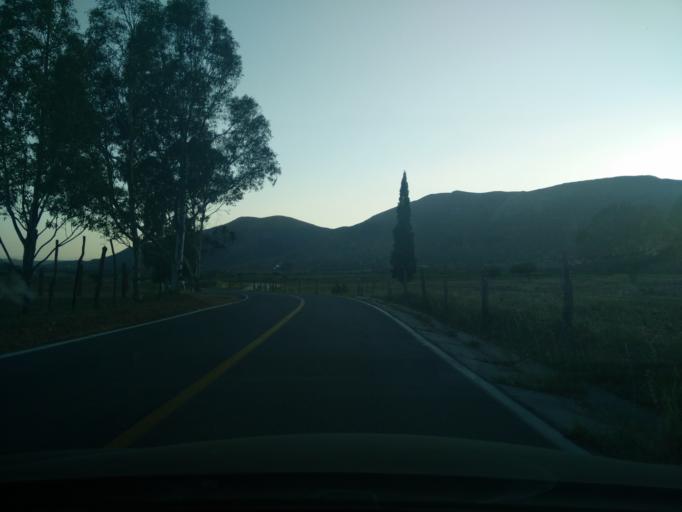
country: MX
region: Baja California
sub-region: Ensenada
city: Rancho Verde
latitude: 32.0482
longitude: -116.6657
